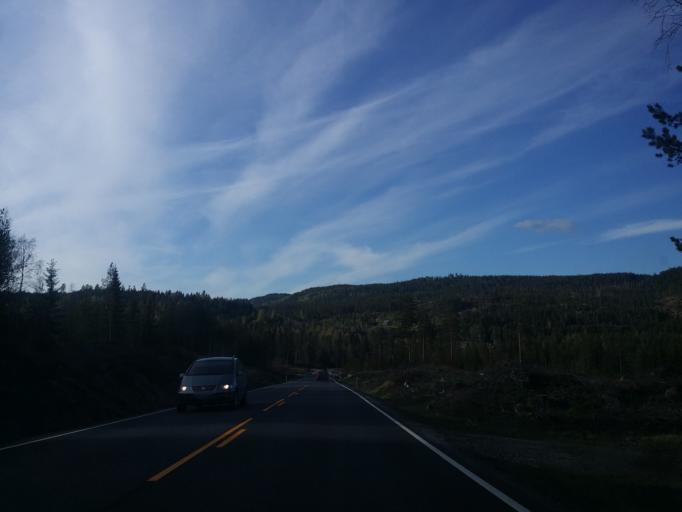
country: NO
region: Buskerud
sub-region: Kongsberg
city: Kongsberg
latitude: 59.6210
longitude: 9.4743
